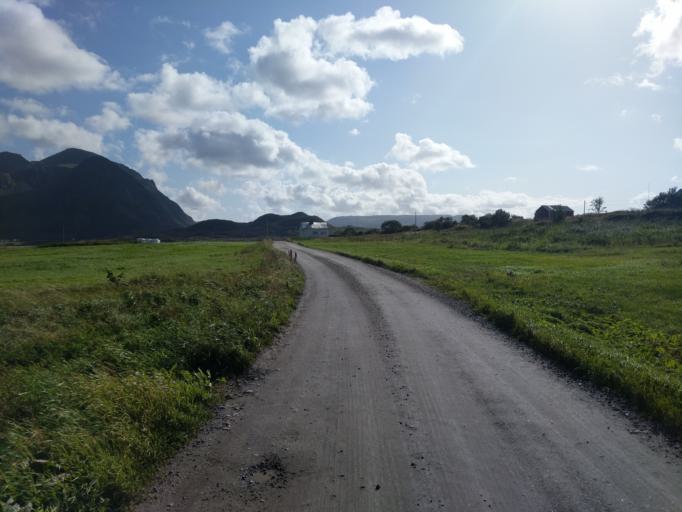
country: NO
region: Nordland
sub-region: Vestvagoy
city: Evjen
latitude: 68.3364
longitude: 13.8864
